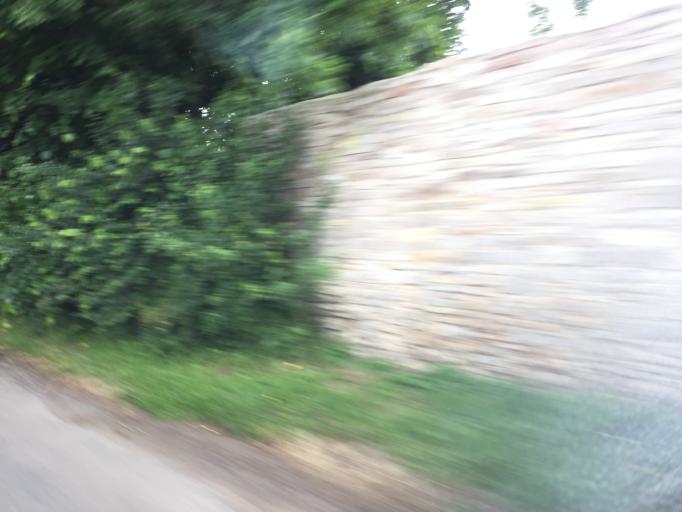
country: GB
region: England
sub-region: South Gloucestershire
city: Tytherington
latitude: 51.5794
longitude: -2.4940
